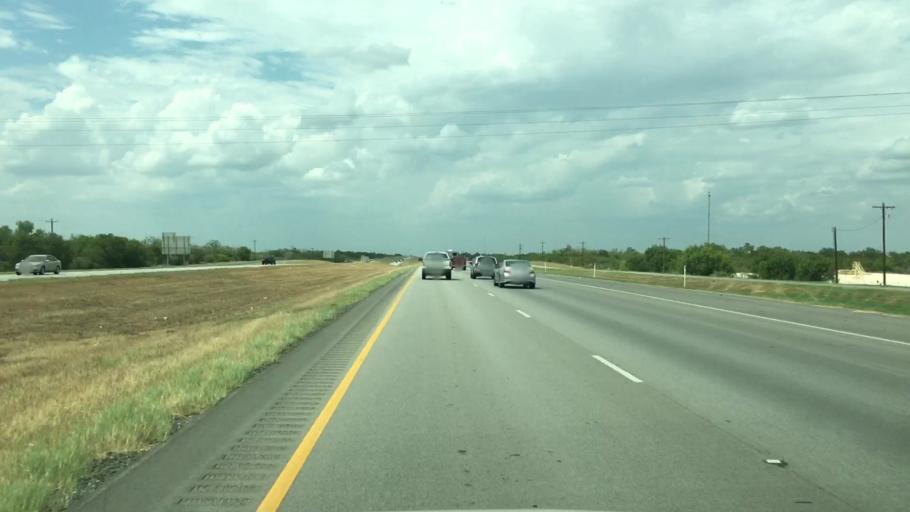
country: US
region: Texas
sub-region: Live Oak County
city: Three Rivers
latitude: 28.5368
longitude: -98.1893
